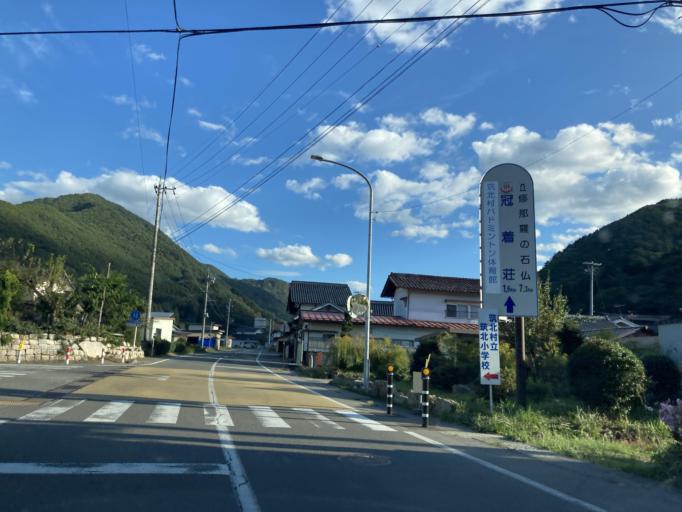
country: JP
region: Nagano
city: Omachi
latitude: 36.4491
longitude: 138.0660
